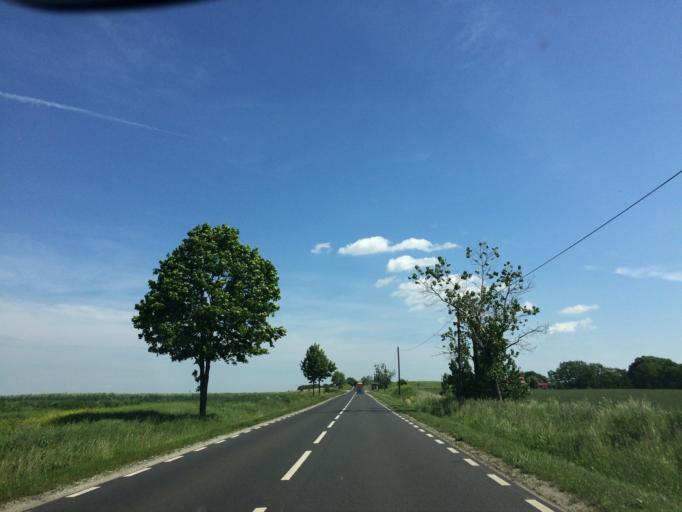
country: PL
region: Lower Silesian Voivodeship
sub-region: Powiat swidnicki
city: Swidnica
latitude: 50.8155
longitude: 16.4953
